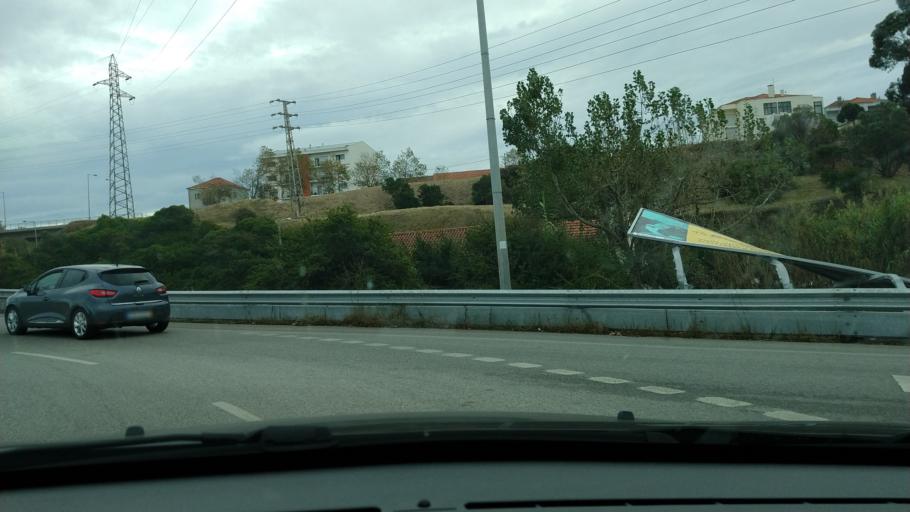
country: PT
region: Coimbra
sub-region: Figueira da Foz
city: Figueira da Foz
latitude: 40.1522
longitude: -8.8472
